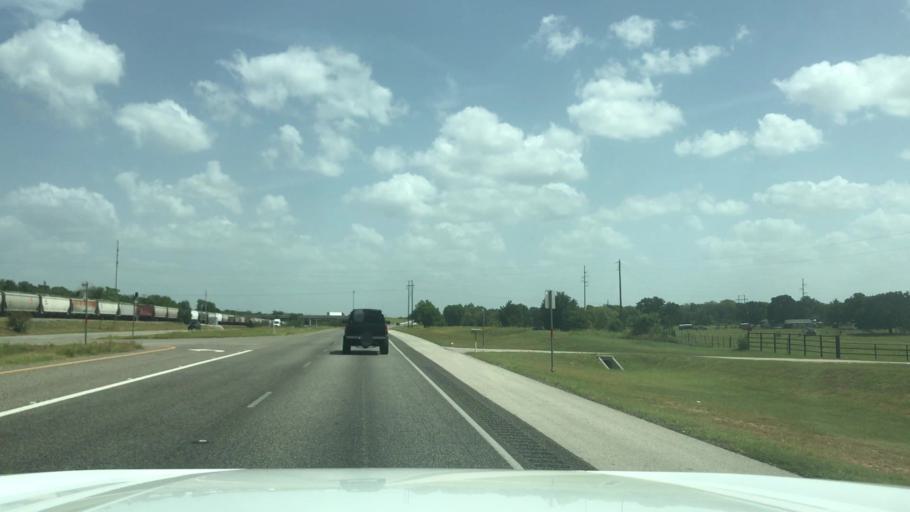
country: US
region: Texas
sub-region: Robertson County
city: Hearne
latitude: 30.9110
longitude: -96.6139
